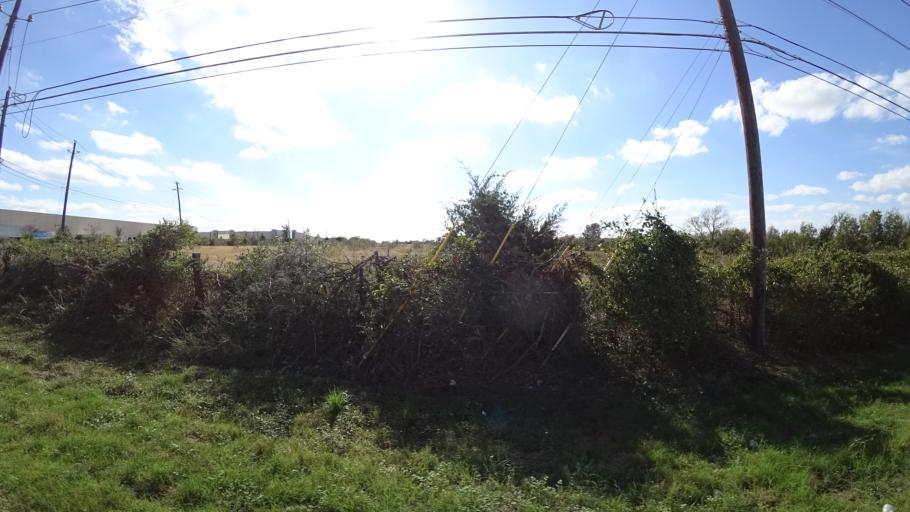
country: US
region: Texas
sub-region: Travis County
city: Wells Branch
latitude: 30.4649
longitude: -97.6736
